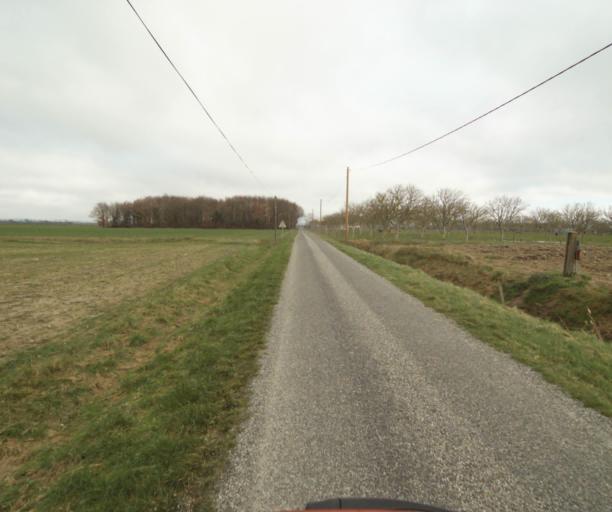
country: FR
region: Midi-Pyrenees
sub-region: Departement de l'Ariege
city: Mazeres
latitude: 43.1819
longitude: 1.6838
